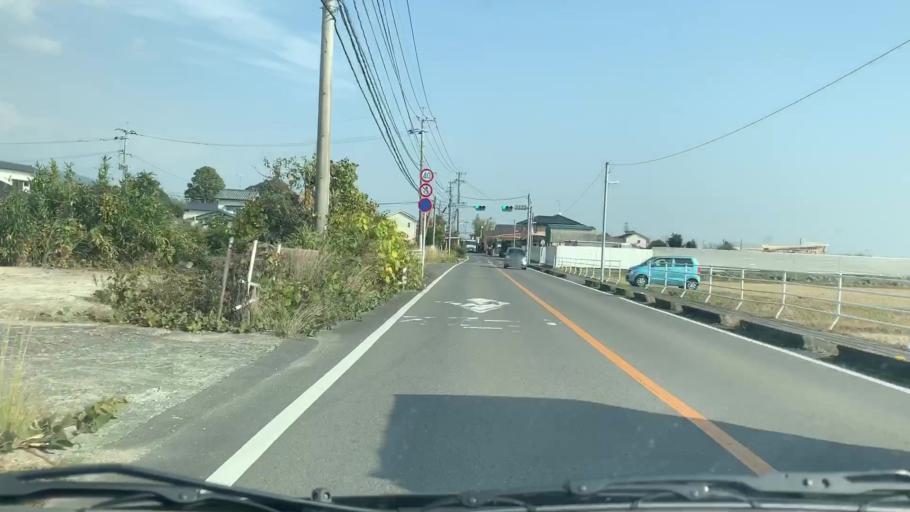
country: JP
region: Saga Prefecture
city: Saga-shi
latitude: 33.3034
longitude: 130.2422
